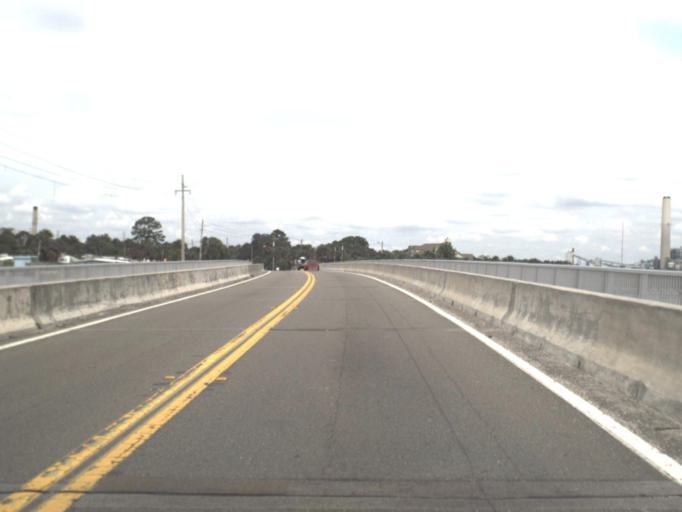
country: US
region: Florida
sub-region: Duval County
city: Jacksonville
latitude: 30.4173
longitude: -81.5304
